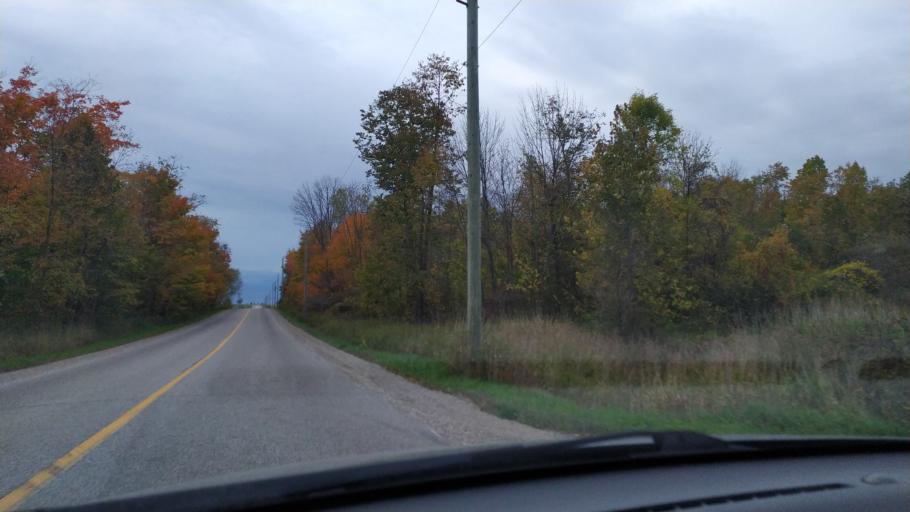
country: CA
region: Ontario
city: Waterloo
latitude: 43.5129
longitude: -80.7453
